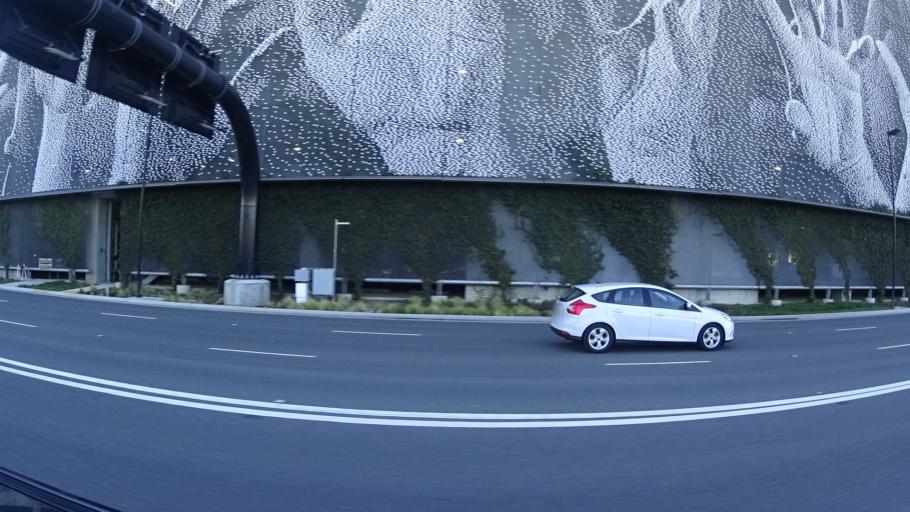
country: US
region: California
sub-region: Santa Clara County
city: Santa Clara
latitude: 37.3654
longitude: -121.9220
